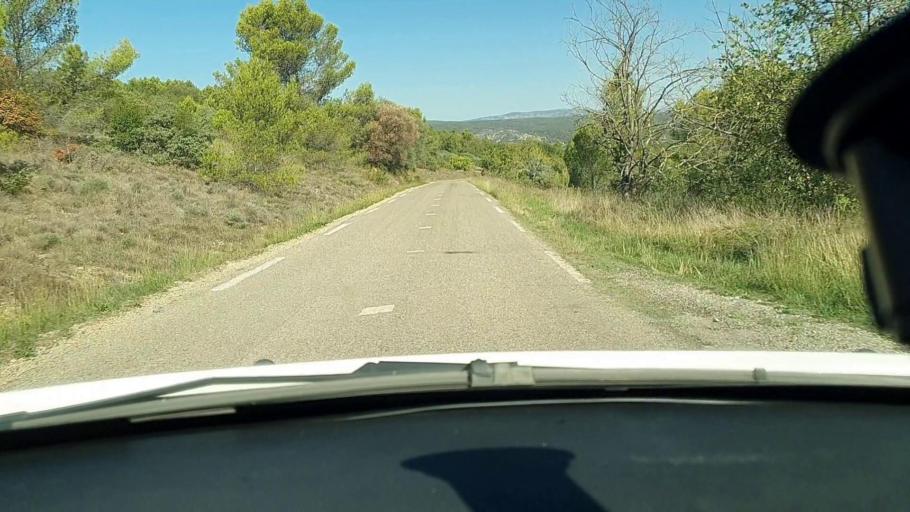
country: FR
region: Languedoc-Roussillon
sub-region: Departement du Gard
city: Saint-Julien-de-Peyrolas
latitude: 44.2652
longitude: 4.5339
